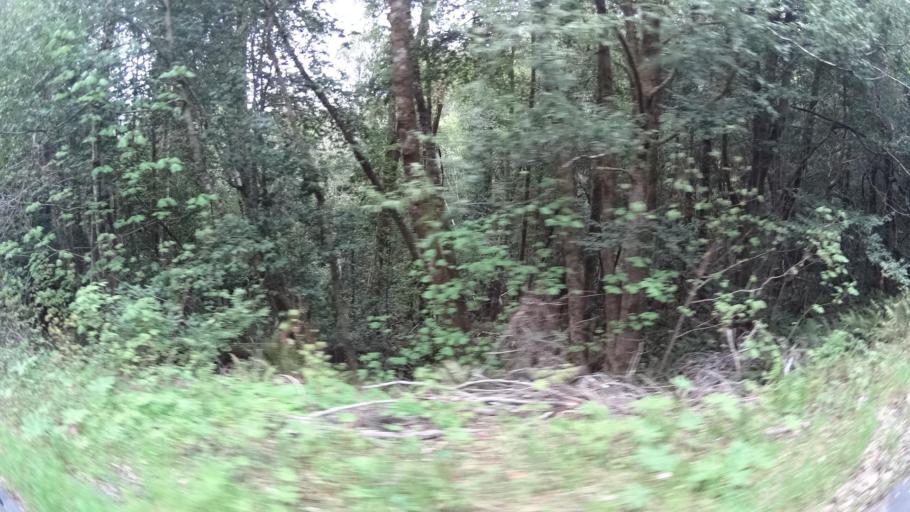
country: US
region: California
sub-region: Humboldt County
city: Blue Lake
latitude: 40.9485
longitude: -123.8423
